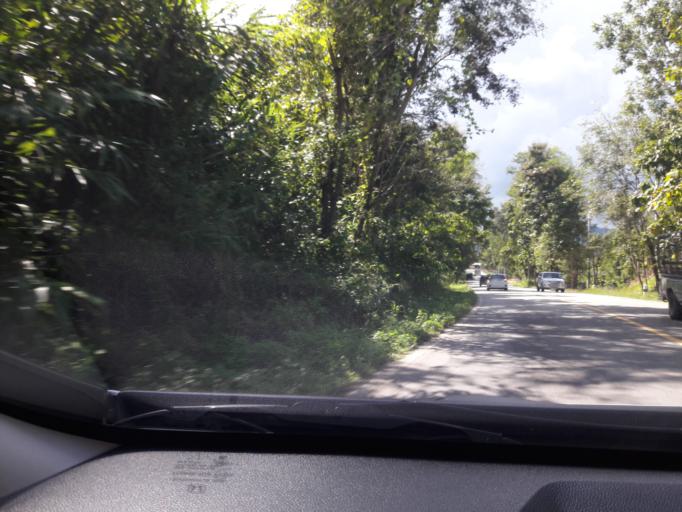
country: TH
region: Mae Hong Son
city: Mae Hi
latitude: 19.3140
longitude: 98.4470
